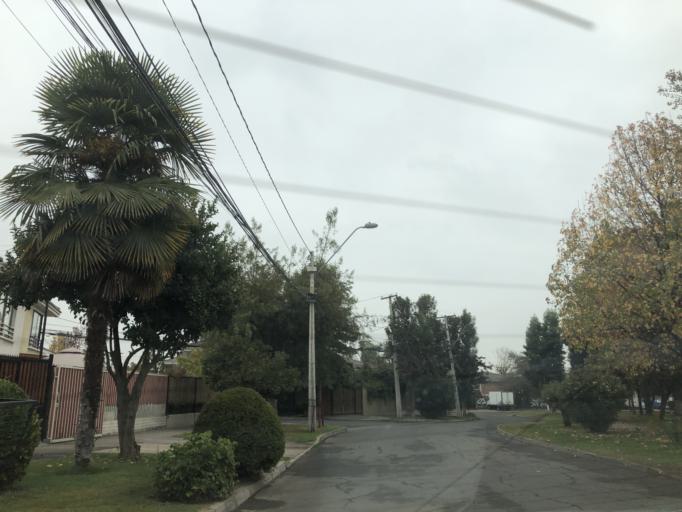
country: CL
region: Santiago Metropolitan
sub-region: Provincia de Cordillera
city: Puente Alto
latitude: -33.5819
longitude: -70.5830
